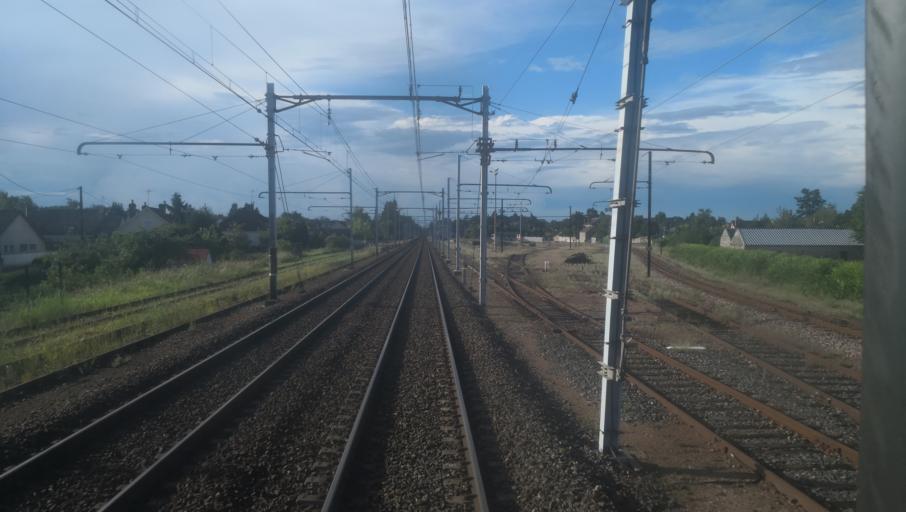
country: FR
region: Centre
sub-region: Departement du Loir-et-Cher
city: Salbris
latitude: 47.4215
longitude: 2.0484
